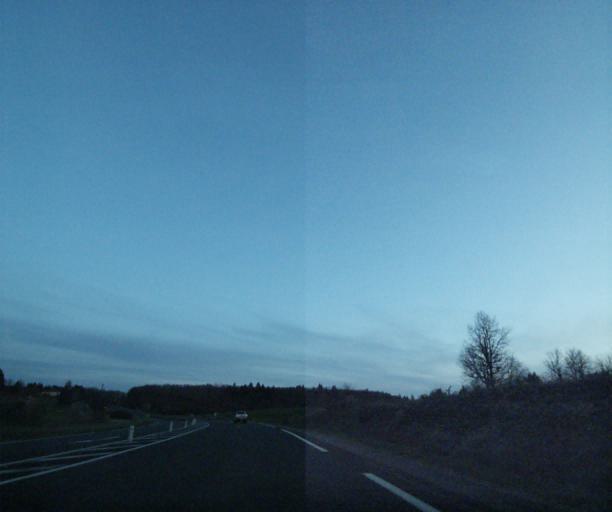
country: FR
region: Midi-Pyrenees
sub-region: Departement du Lot
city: Pradines
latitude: 44.5128
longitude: 1.4438
